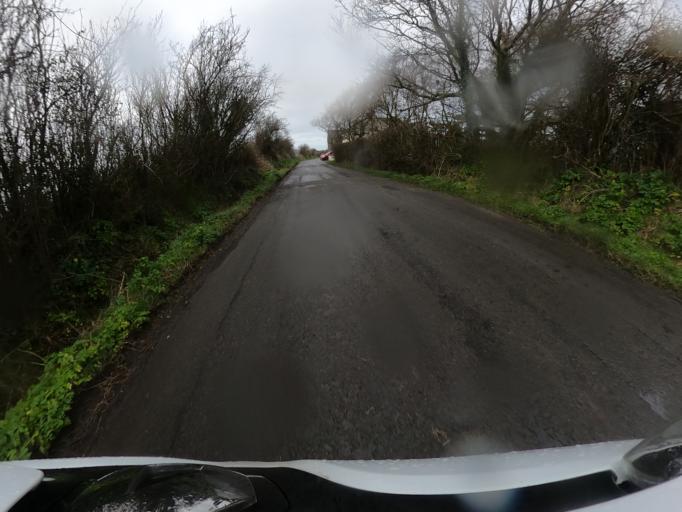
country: IM
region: Ramsey
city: Ramsey
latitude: 54.3709
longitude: -4.4470
